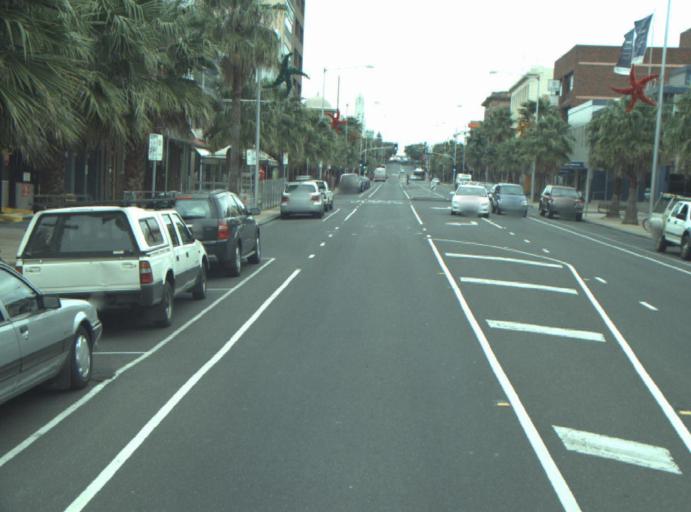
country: AU
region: Victoria
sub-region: Greater Geelong
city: Geelong
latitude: -38.1455
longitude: 144.3616
